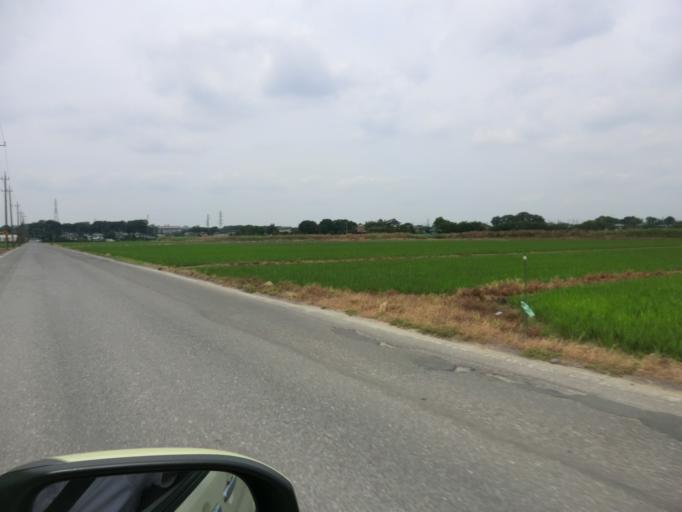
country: JP
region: Ibaraki
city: Iwai
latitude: 36.0688
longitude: 139.9358
